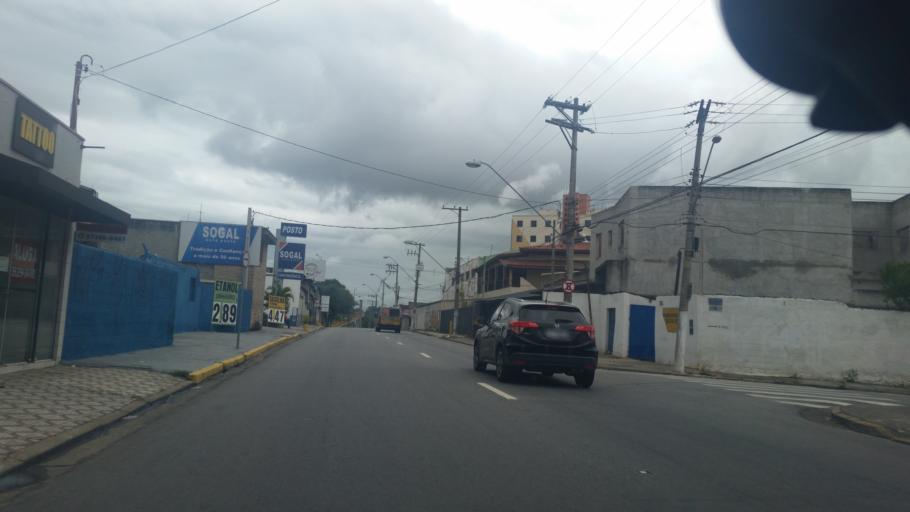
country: BR
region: Sao Paulo
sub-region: Taubate
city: Taubate
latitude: -23.0416
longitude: -45.5745
